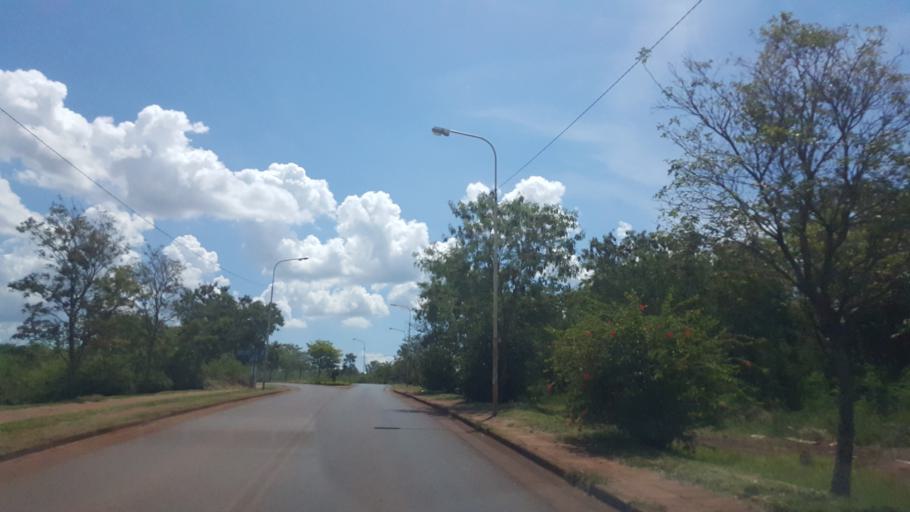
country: AR
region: Misiones
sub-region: Departamento de Capital
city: Posadas
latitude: -27.3731
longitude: -55.9591
